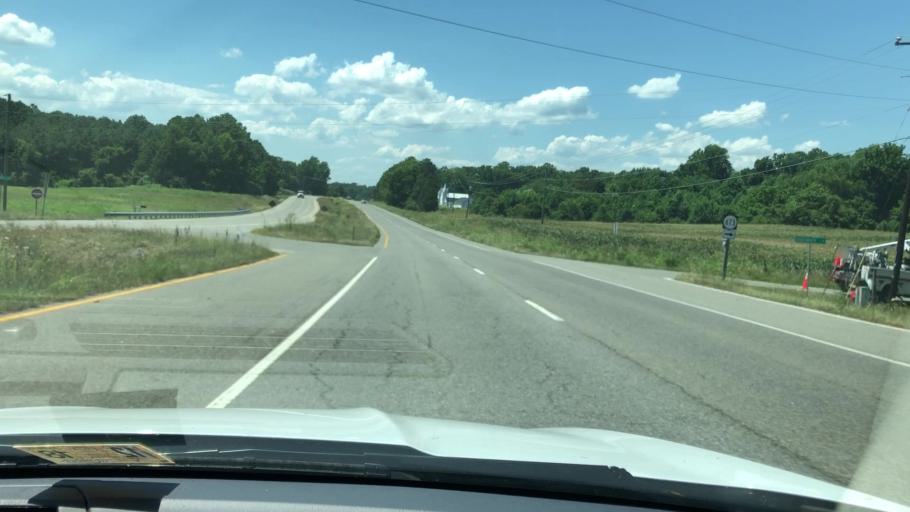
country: US
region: Virginia
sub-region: Middlesex County
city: Saluda
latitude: 37.6064
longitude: -76.5399
